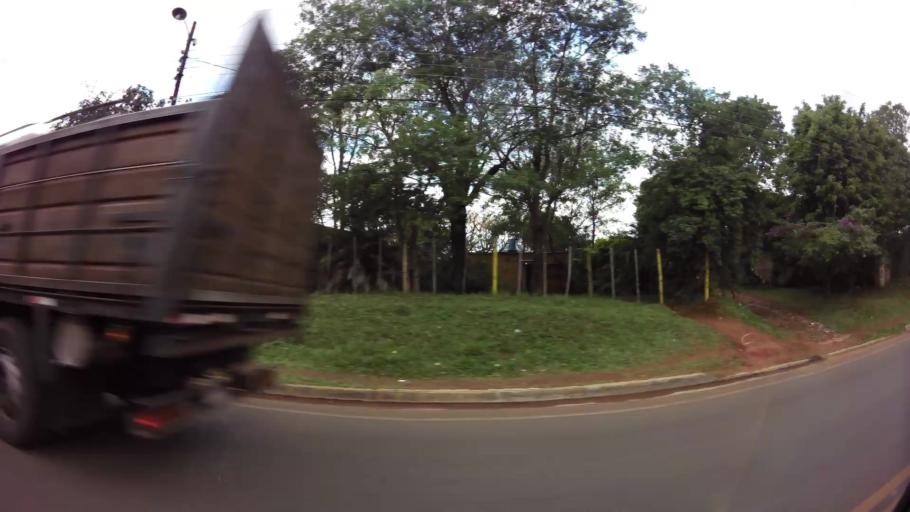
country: PY
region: Central
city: San Lorenzo
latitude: -25.2896
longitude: -57.4824
